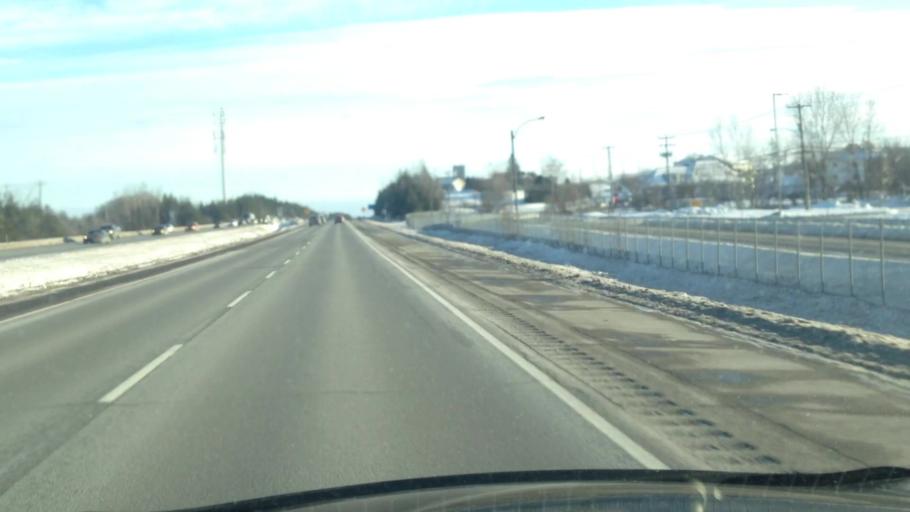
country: CA
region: Quebec
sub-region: Laurentides
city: Saint-Jerome
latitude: 45.8109
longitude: -74.0447
